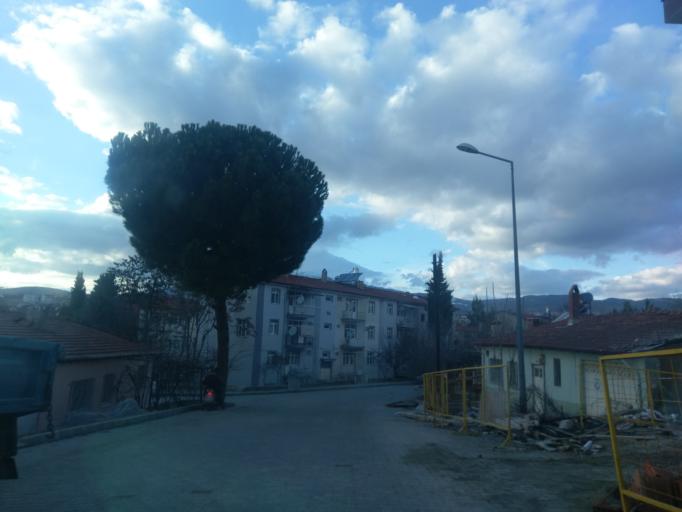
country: TR
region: Kuetahya
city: Gediz
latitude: 38.9925
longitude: 29.3869
